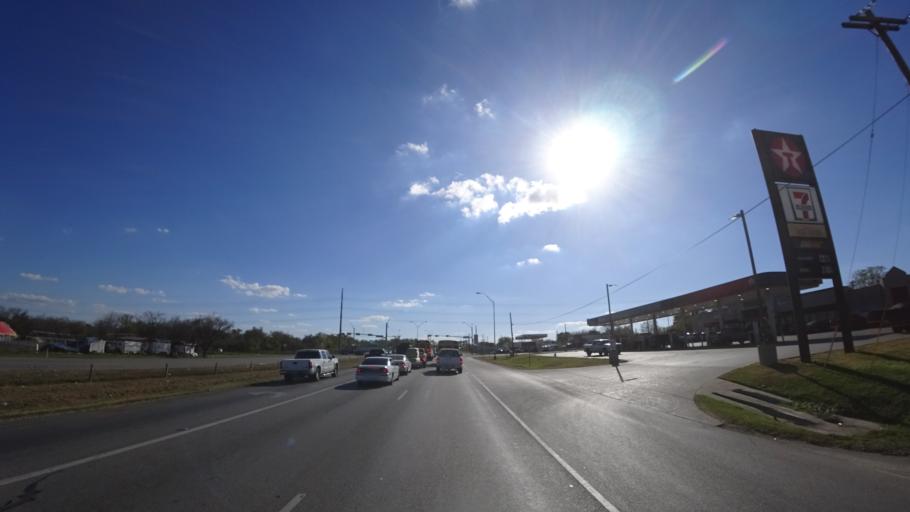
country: US
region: Texas
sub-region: Travis County
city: Onion Creek
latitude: 30.1653
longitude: -97.6927
